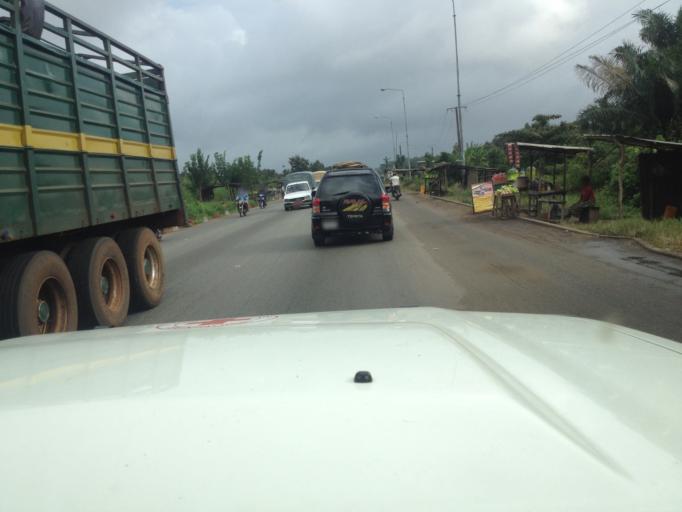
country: BJ
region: Queme
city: Porto-Novo
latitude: 6.4426
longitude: 2.6223
